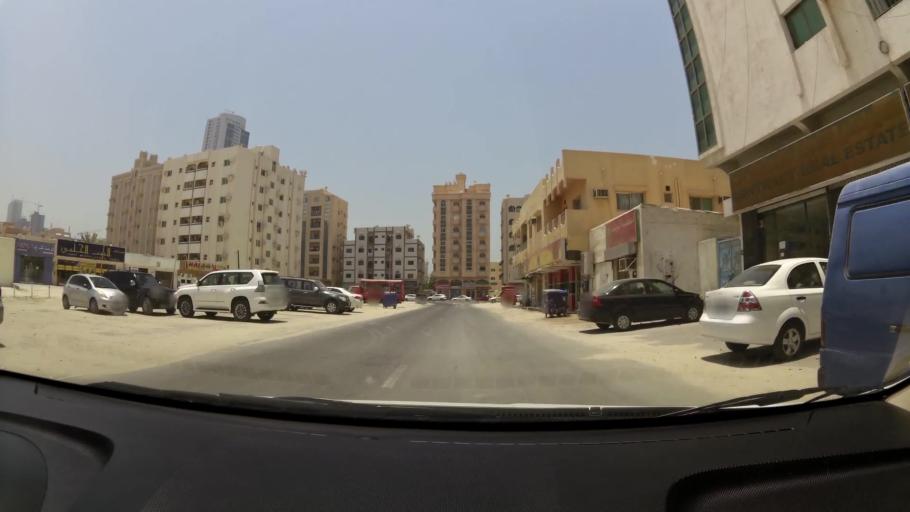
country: AE
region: Ajman
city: Ajman
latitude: 25.4116
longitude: 55.4394
